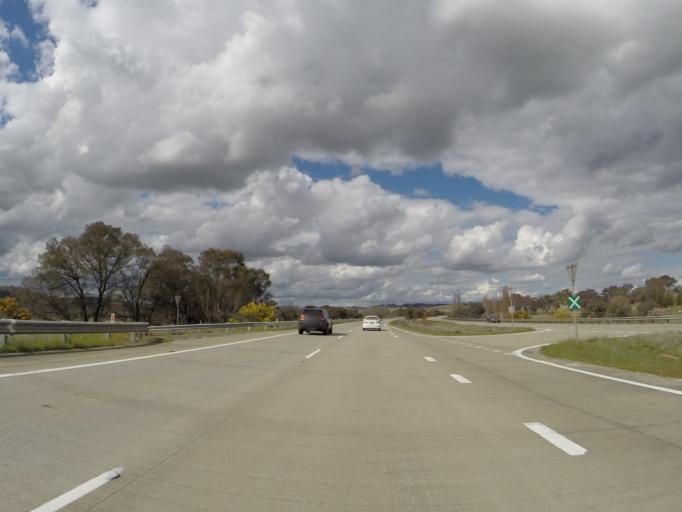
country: AU
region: New South Wales
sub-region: Yass Valley
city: Murrumbateman
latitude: -34.7866
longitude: 149.1816
